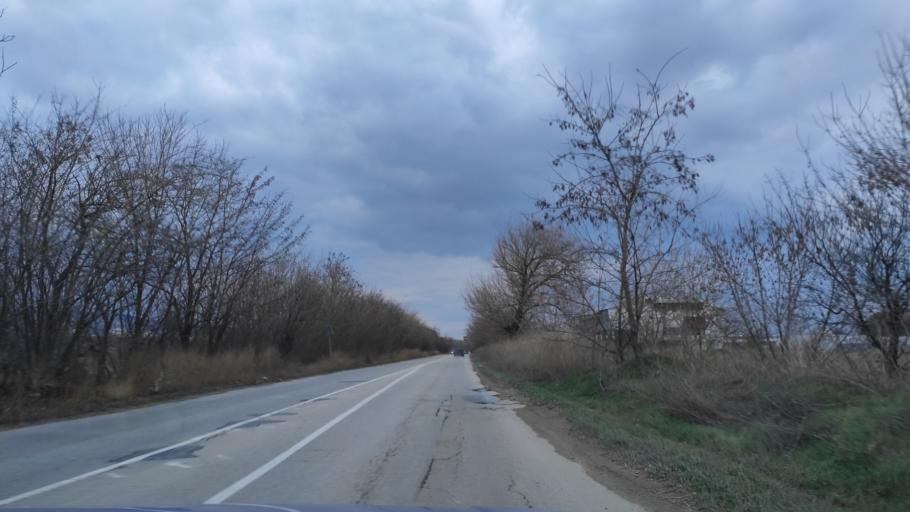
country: BG
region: Varna
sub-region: Obshtina Aksakovo
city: Aksakovo
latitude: 43.2280
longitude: 27.8454
